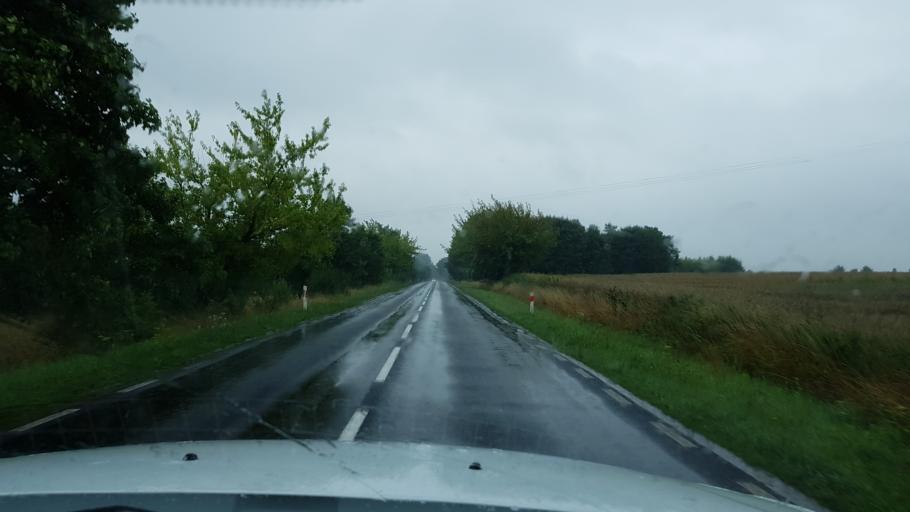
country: PL
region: West Pomeranian Voivodeship
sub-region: Powiat kolobrzeski
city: Grzybowo
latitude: 54.1080
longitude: 15.5244
